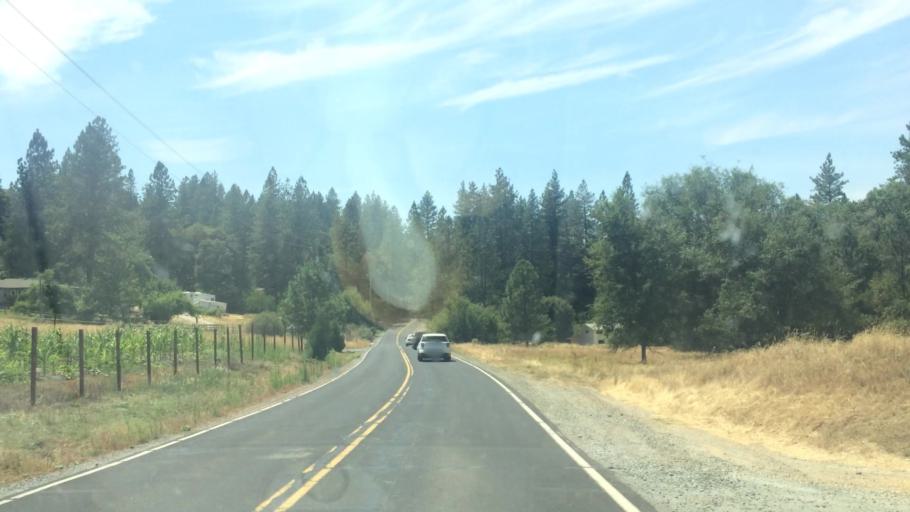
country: US
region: California
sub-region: Amador County
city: Pine Grove
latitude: 38.4157
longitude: -120.6896
